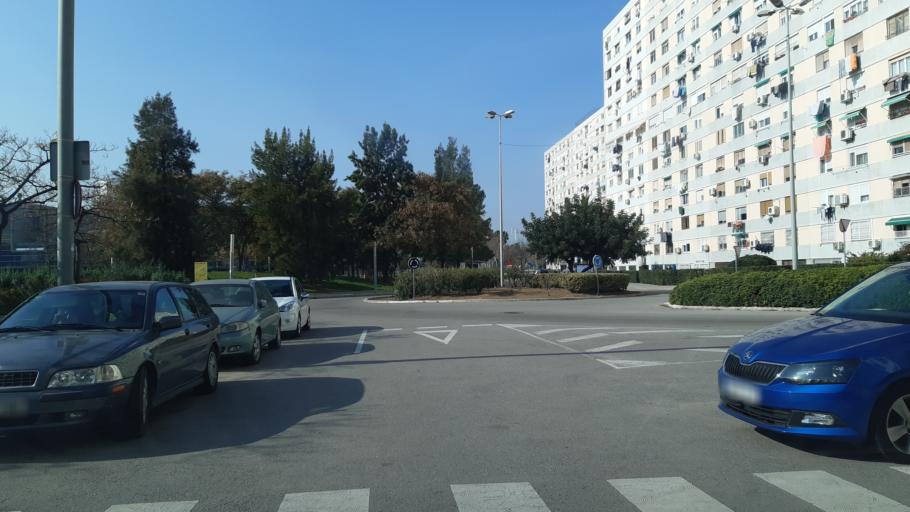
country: ES
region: Catalonia
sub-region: Provincia de Barcelona
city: L'Hospitalet de Llobregat
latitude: 41.3474
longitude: 2.1095
